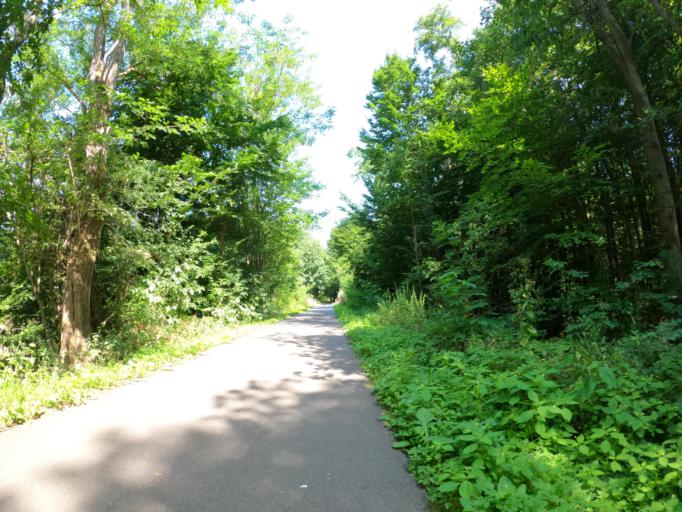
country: DE
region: Brandenburg
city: Templin
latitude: 53.2343
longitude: 13.5022
